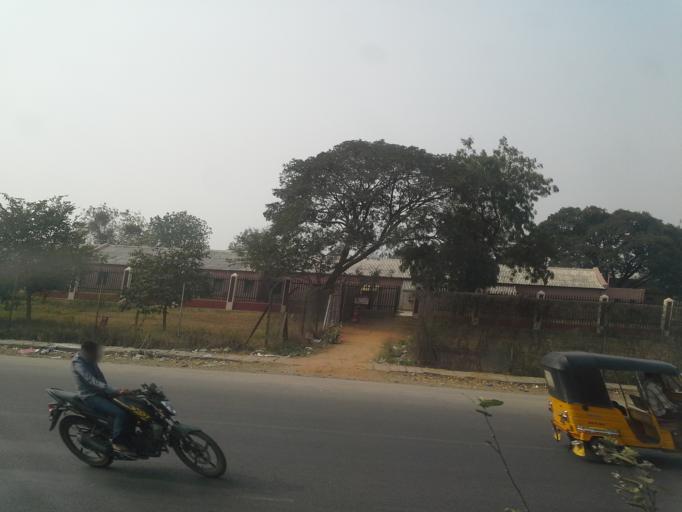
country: IN
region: Telangana
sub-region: Medak
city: Patancheru
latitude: 17.5192
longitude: 78.2781
